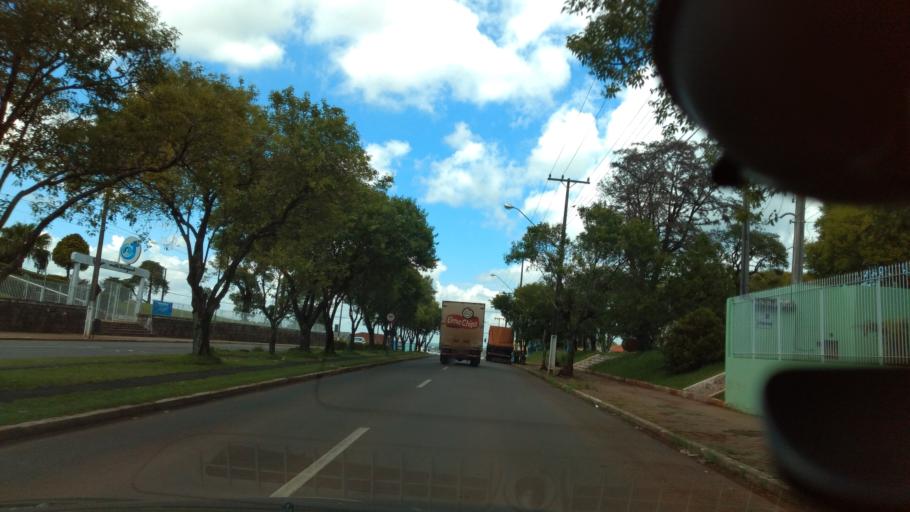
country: BR
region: Parana
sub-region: Guarapuava
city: Guarapuava
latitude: -25.3906
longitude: -51.4781
